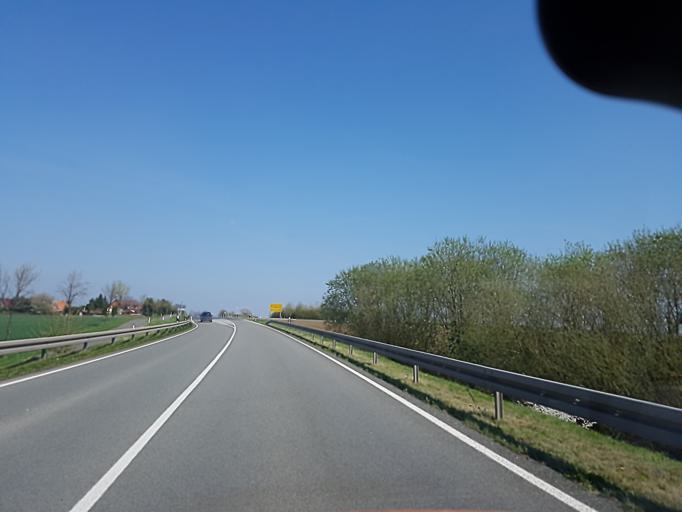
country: DE
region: Saxony
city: Mutzschen
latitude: 51.2490
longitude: 12.8805
